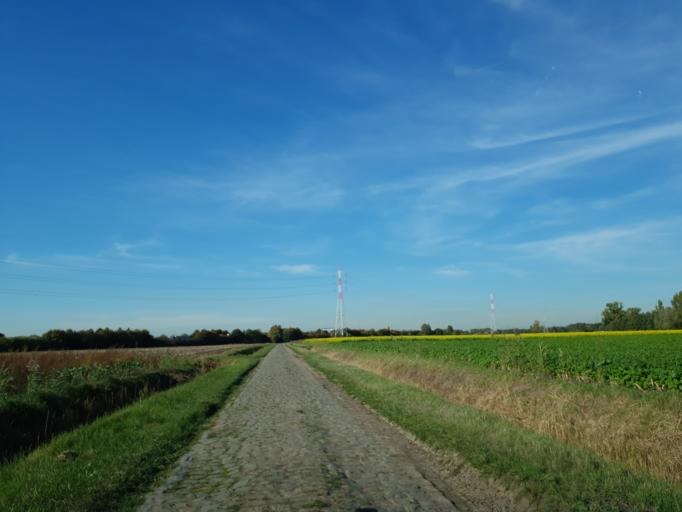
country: BE
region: Flanders
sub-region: Provincie Antwerpen
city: Stabroek
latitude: 51.3355
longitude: 4.3509
